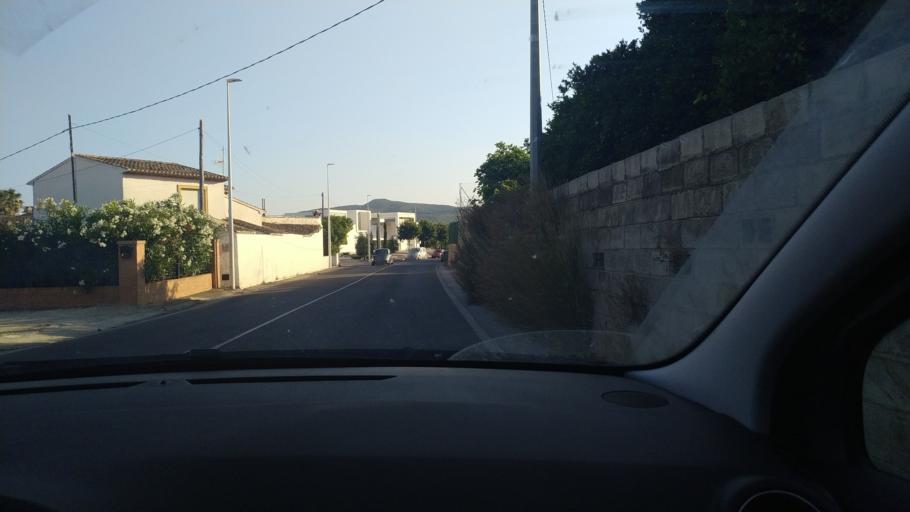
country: ES
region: Valencia
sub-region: Provincia de Alicante
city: Javea
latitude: 38.7816
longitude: 0.1552
